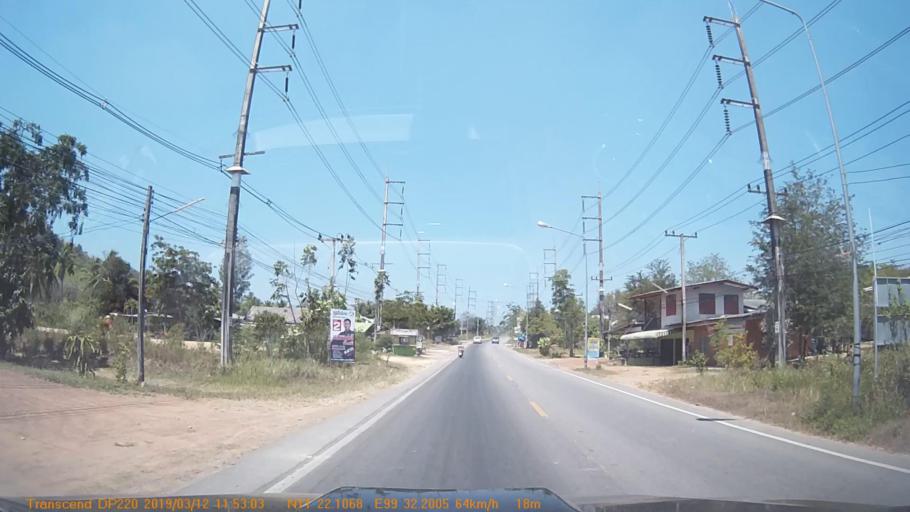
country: TH
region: Prachuap Khiri Khan
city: Thap Sakae
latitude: 11.3685
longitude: 99.5367
